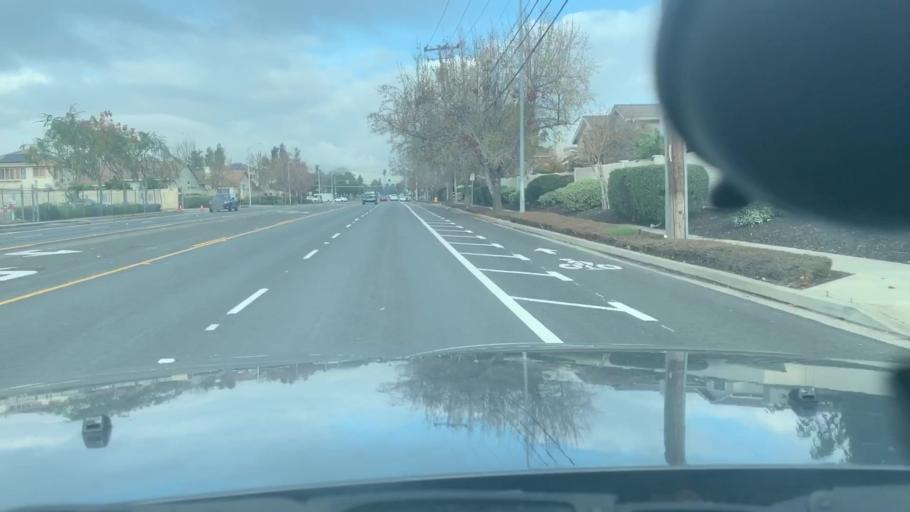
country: US
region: California
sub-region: Alameda County
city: Fremont
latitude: 37.5420
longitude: -122.0154
